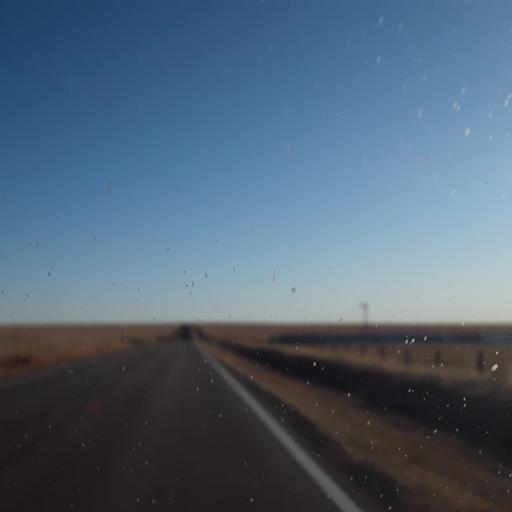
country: US
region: Kansas
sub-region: Wallace County
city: Sharon Springs
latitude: 39.0339
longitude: -101.7386
